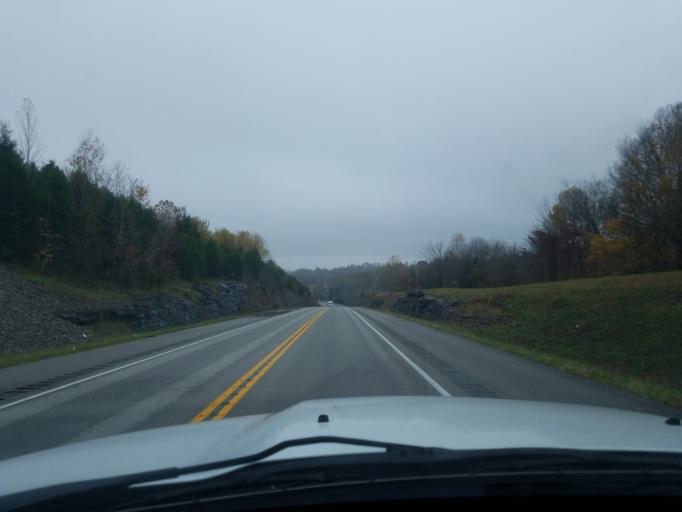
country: US
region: Kentucky
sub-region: Taylor County
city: Campbellsville
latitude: 37.3883
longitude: -85.4234
